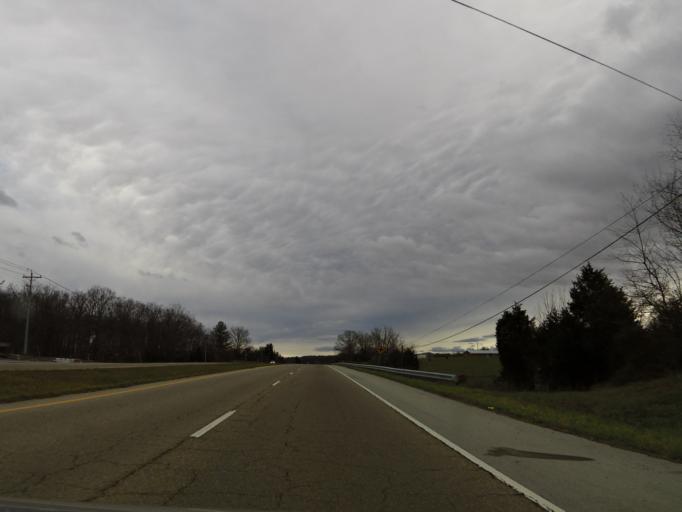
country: US
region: Tennessee
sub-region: Washington County
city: Jonesborough
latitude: 36.2565
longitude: -82.5811
